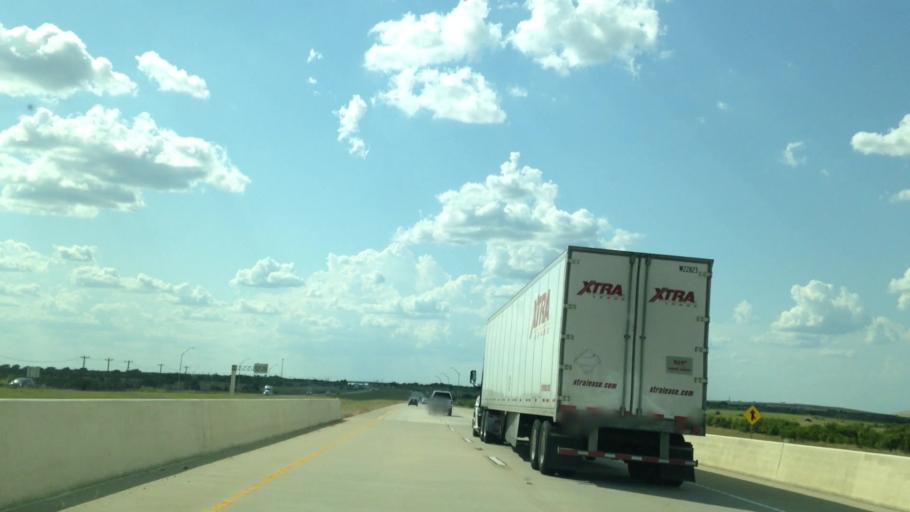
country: US
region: Texas
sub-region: Travis County
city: Onion Creek
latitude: 30.0847
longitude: -97.7369
